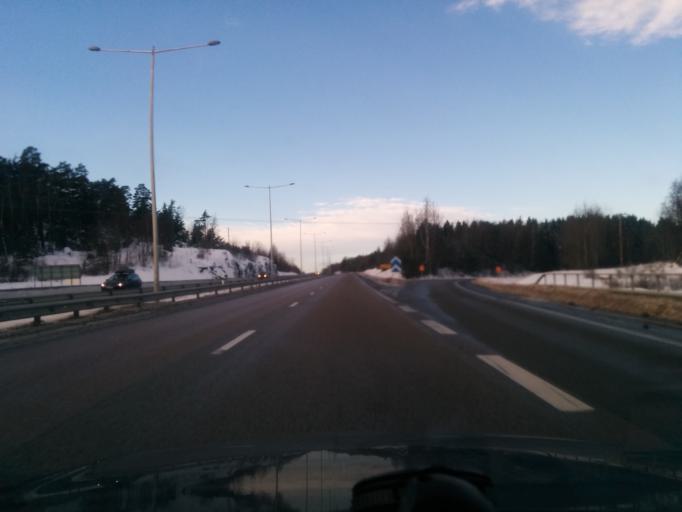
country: SE
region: Stockholm
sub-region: Upplands-Bro Kommun
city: Bro
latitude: 59.5313
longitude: 17.6311
